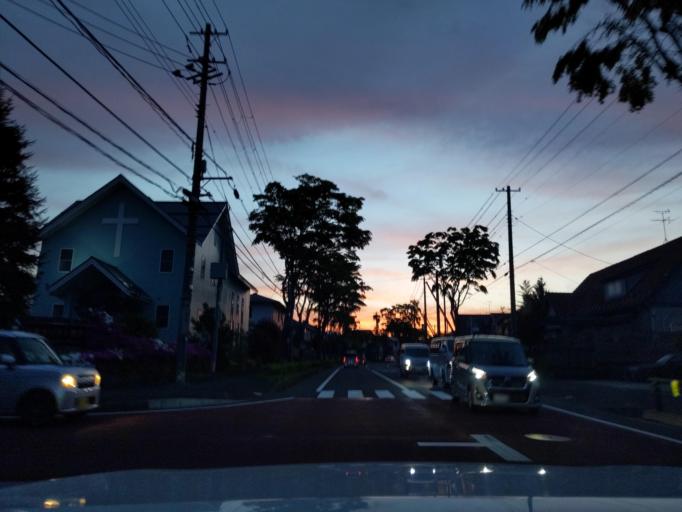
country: JP
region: Miyagi
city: Tomiya
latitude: 38.3775
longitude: 140.8685
